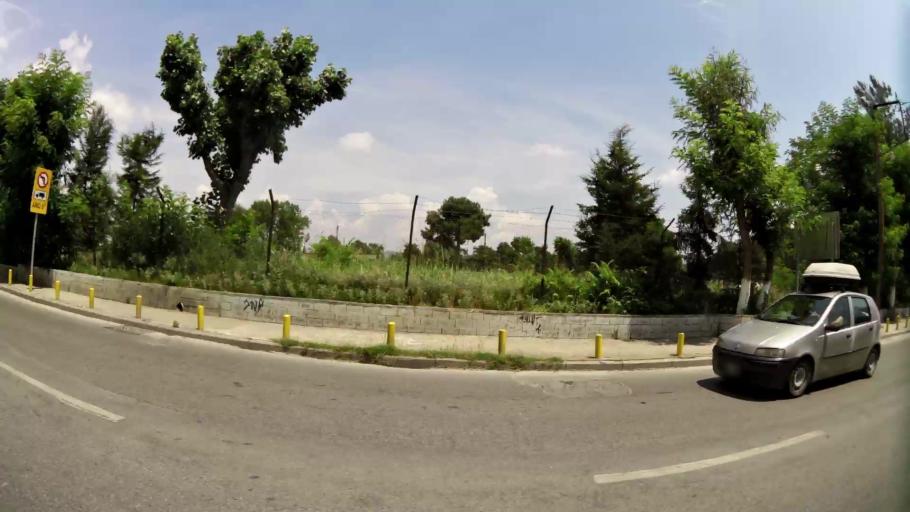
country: GR
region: Central Macedonia
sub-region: Nomos Thessalonikis
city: Ampelokipoi
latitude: 40.6575
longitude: 22.9144
